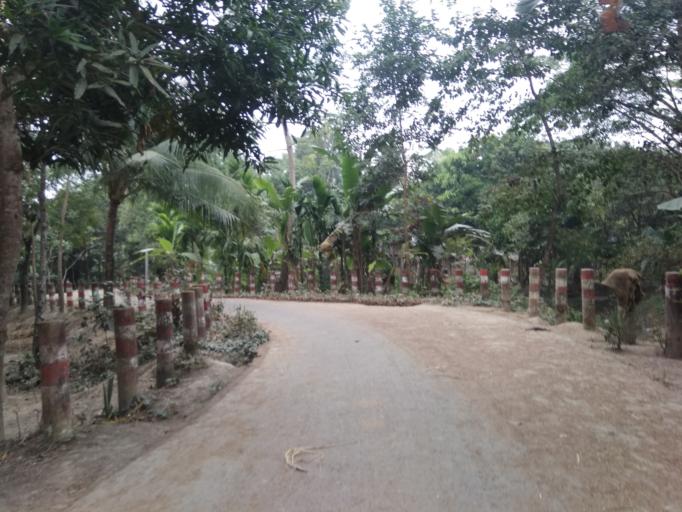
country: BD
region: Barisal
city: Mehendiganj
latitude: 22.9195
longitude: 90.3913
